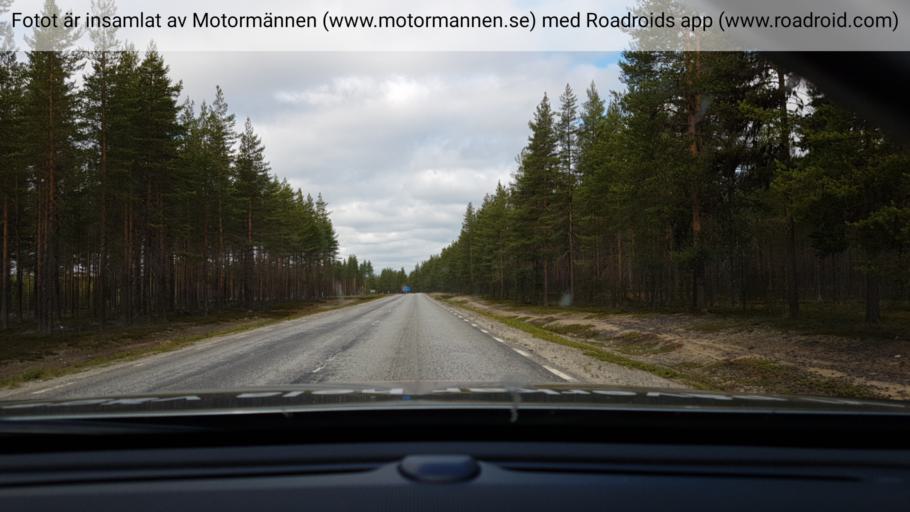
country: SE
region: Vaesterbotten
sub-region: Lycksele Kommun
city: Lycksele
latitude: 64.8239
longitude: 18.8116
